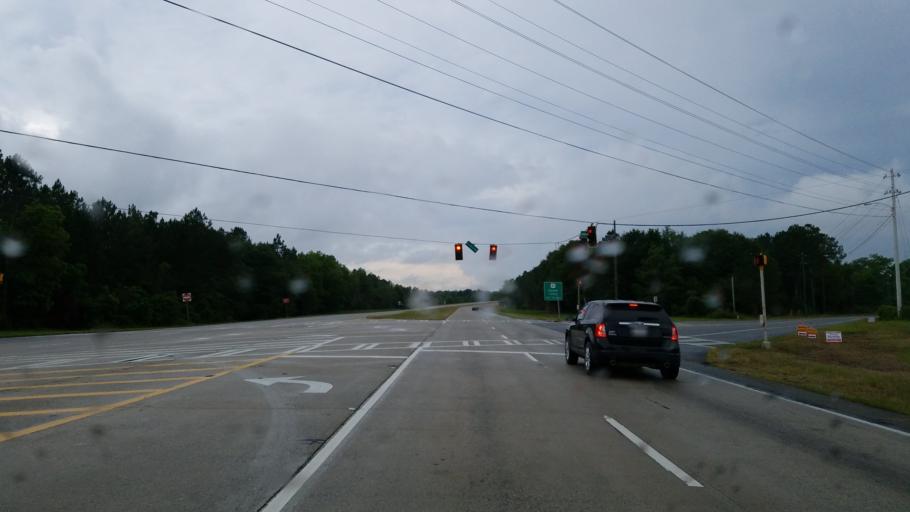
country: US
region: Georgia
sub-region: Crisp County
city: Cordele
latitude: 31.9266
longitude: -83.7601
